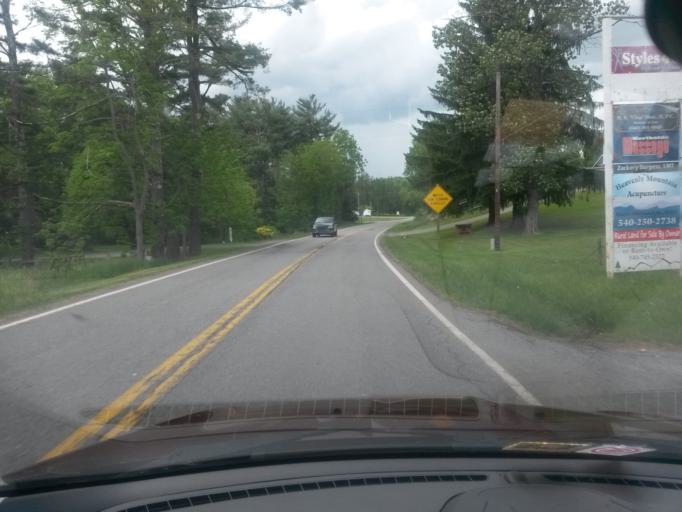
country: US
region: Virginia
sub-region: Floyd County
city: Floyd
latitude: 36.9172
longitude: -80.3231
